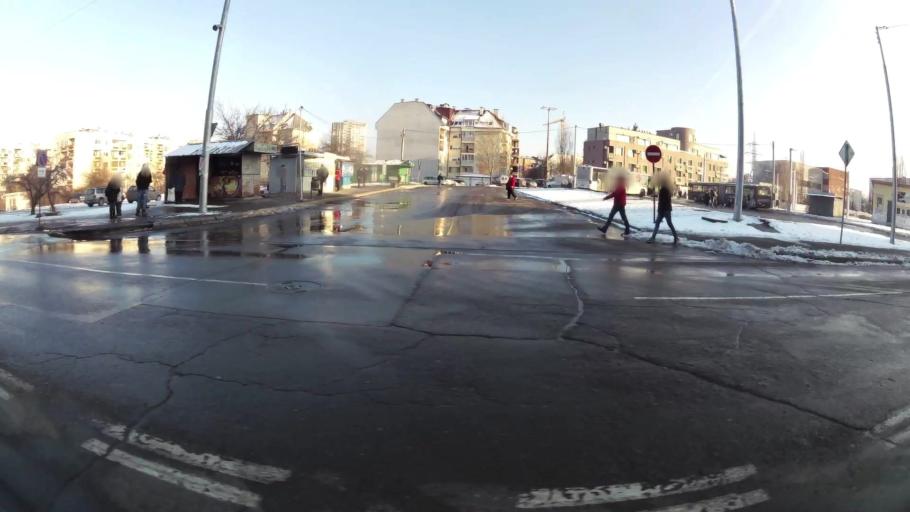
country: BG
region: Sofia-Capital
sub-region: Stolichna Obshtina
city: Sofia
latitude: 42.6780
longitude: 23.3701
